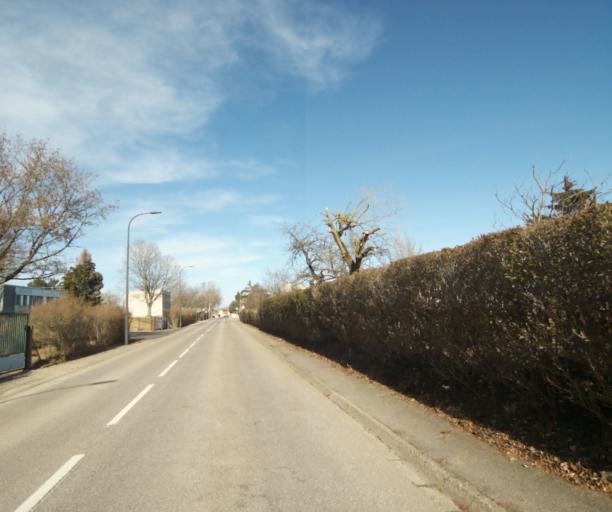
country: FR
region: Lorraine
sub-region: Departement de Meurthe-et-Moselle
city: Villers-les-Nancy
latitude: 48.6638
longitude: 6.1402
